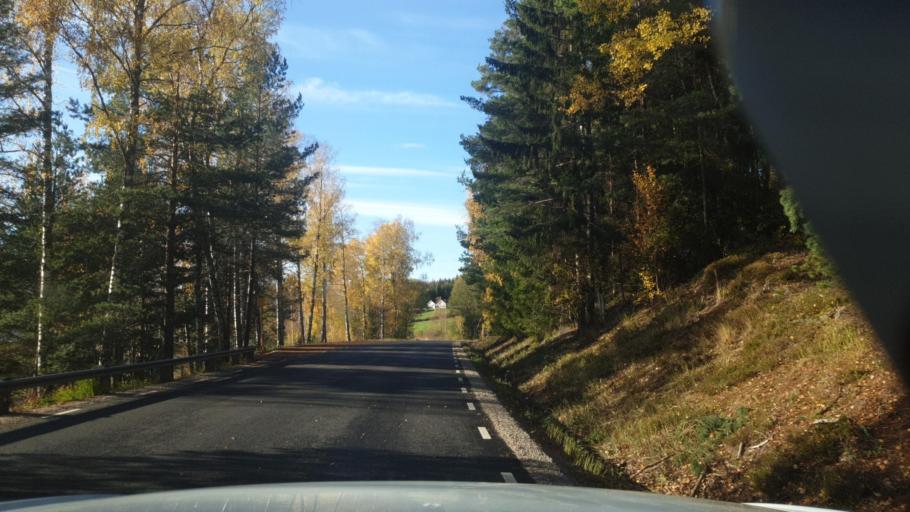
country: SE
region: Vaermland
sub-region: Arvika Kommun
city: Arvika
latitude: 59.6623
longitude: 12.6975
